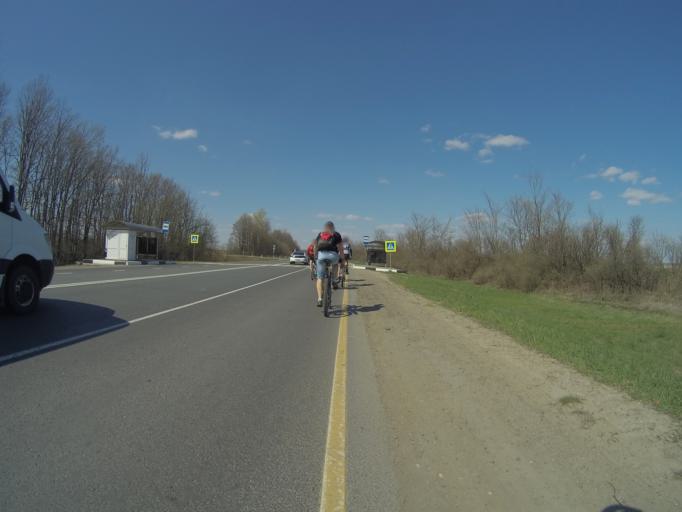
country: RU
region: Vladimir
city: Suzdal'
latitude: 56.3752
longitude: 40.4607
